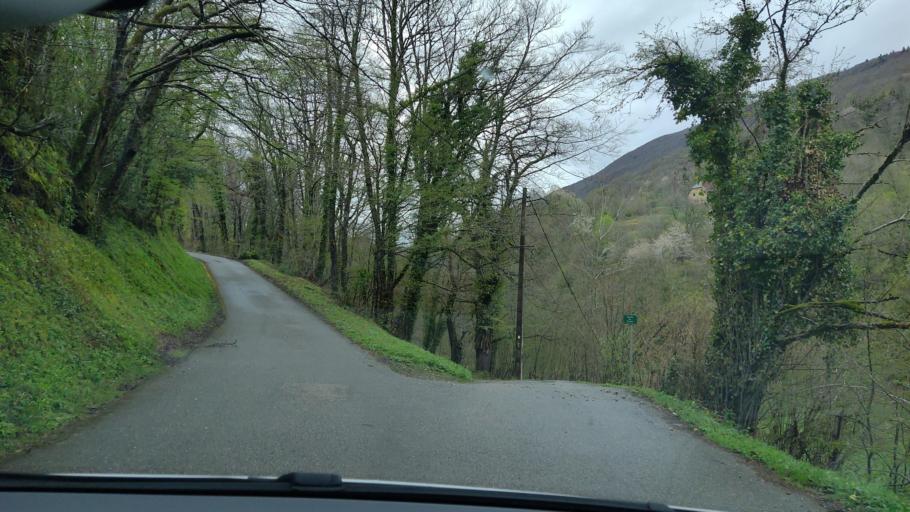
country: FR
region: Rhone-Alpes
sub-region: Departement de la Savoie
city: Vimines
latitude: 45.5476
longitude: 5.8182
